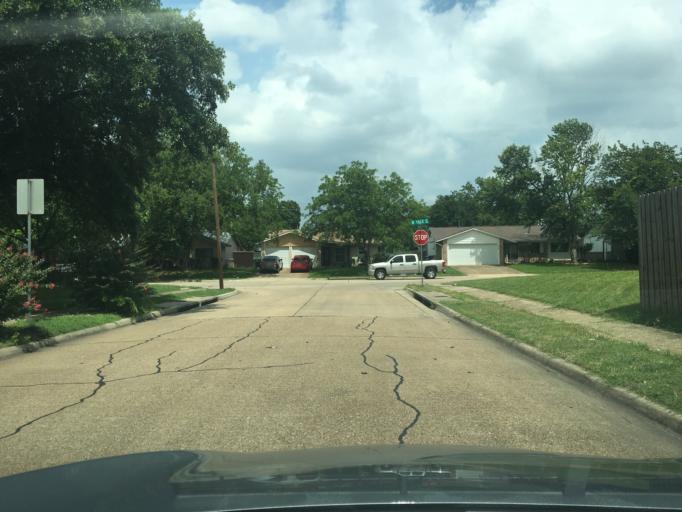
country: US
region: Texas
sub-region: Dallas County
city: Richardson
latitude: 32.9151
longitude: -96.6927
